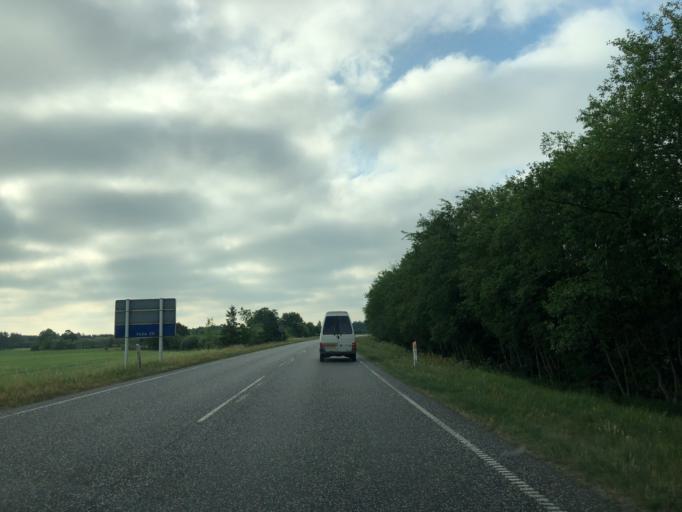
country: DK
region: South Denmark
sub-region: Vejle Kommune
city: Give
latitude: 55.7537
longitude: 9.3122
